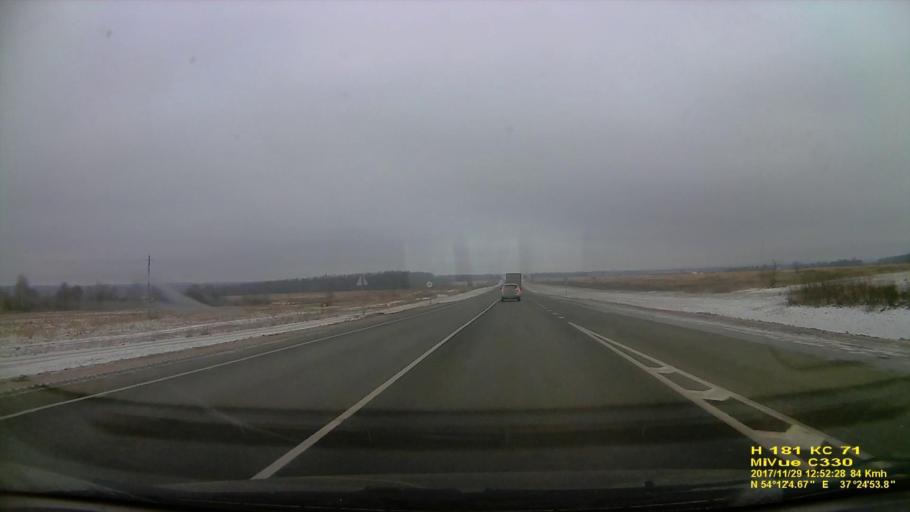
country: RU
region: Tula
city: Barsuki
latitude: 54.2014
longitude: 37.4149
